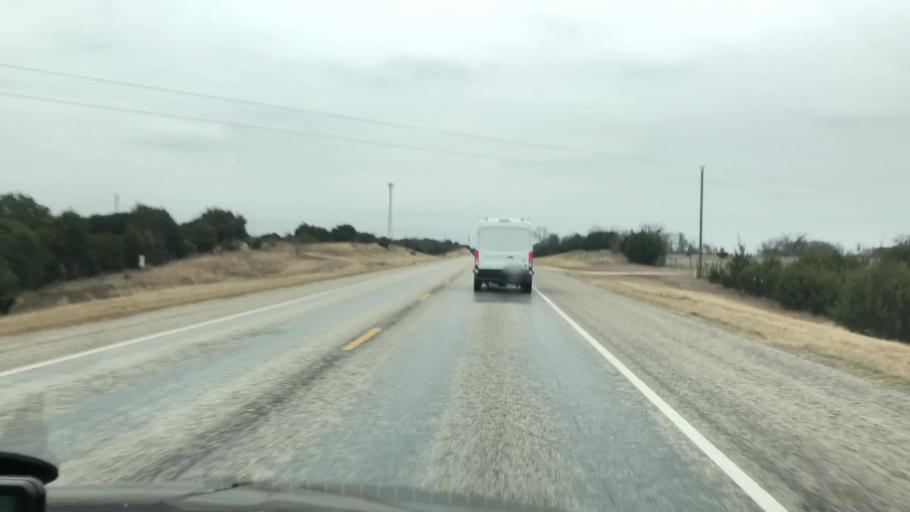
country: US
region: Texas
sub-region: Lampasas County
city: Lampasas
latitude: 31.1272
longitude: -98.1894
